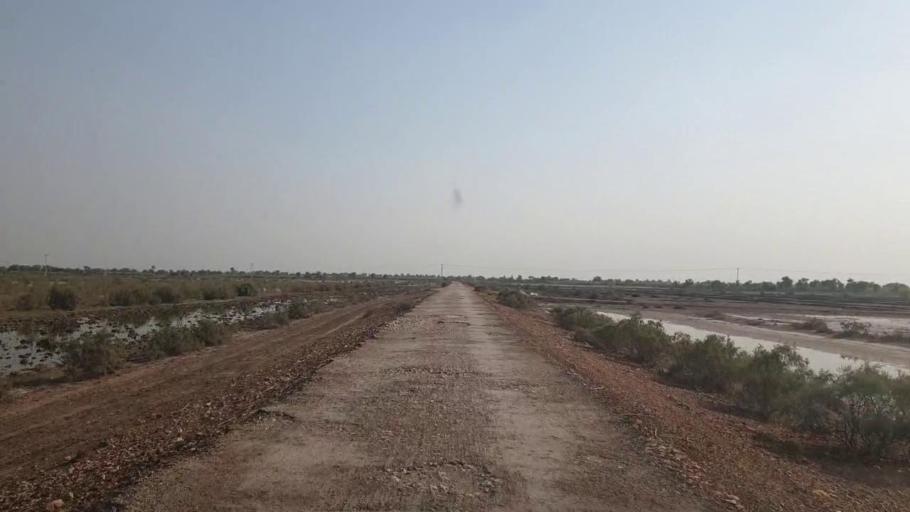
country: PK
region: Sindh
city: Sanghar
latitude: 26.0513
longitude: 68.8971
